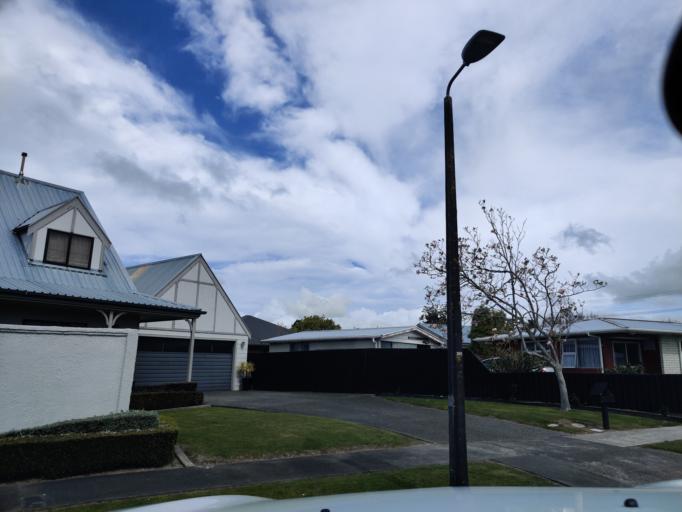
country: NZ
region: Manawatu-Wanganui
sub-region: Palmerston North City
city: Palmerston North
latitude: -40.3618
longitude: 175.5816
